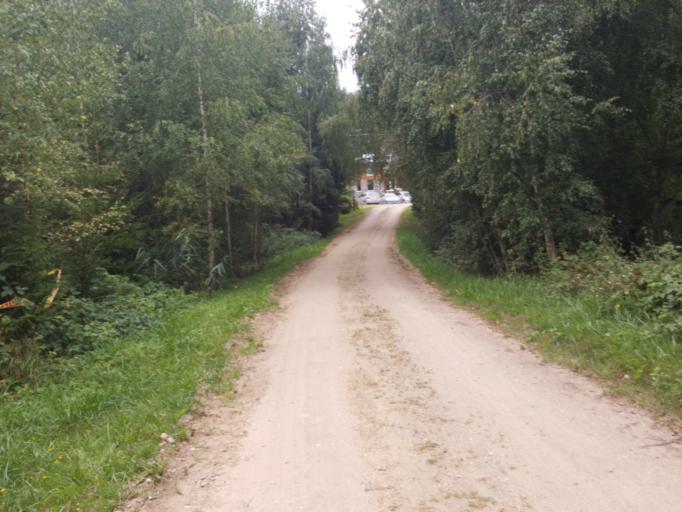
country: LT
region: Alytaus apskritis
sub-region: Alytus
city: Alytus
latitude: 54.2682
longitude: 24.0905
